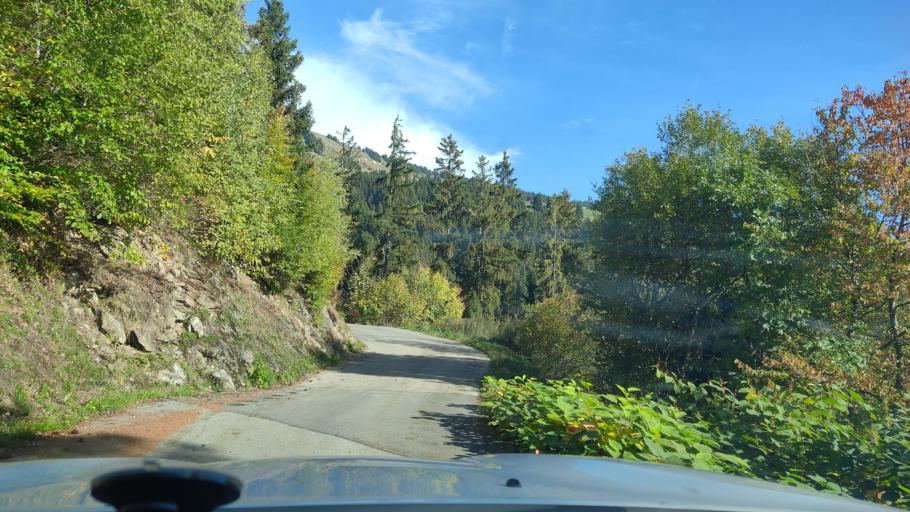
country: FR
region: Rhone-Alpes
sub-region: Departement de la Savoie
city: Beaufort
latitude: 45.7309
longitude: 6.5084
